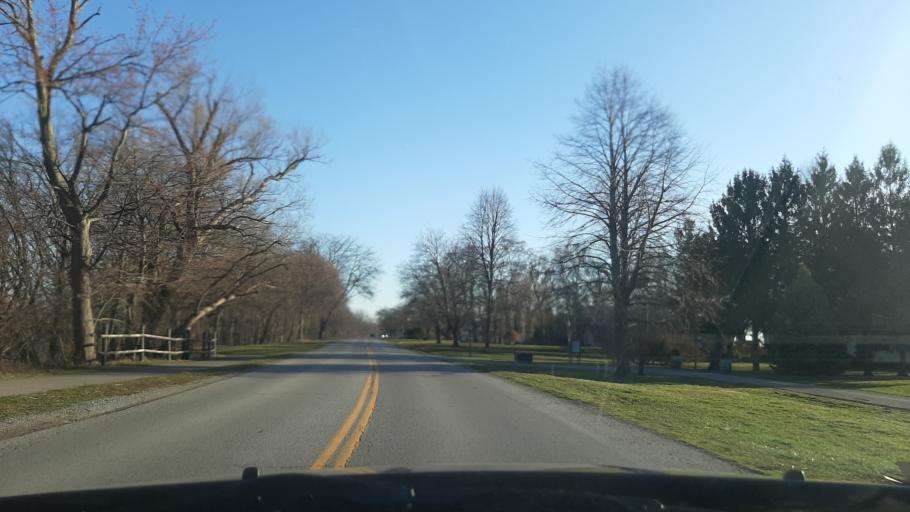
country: US
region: New York
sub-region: Niagara County
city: Youngstown
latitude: 43.2160
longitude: -79.0606
